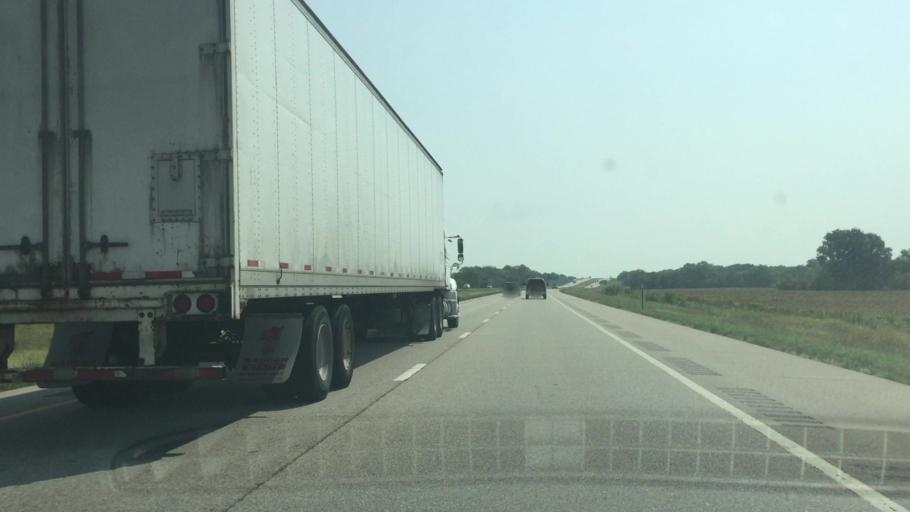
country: US
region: Kansas
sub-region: Lyon County
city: Emporia
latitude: 38.4110
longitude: -96.1146
